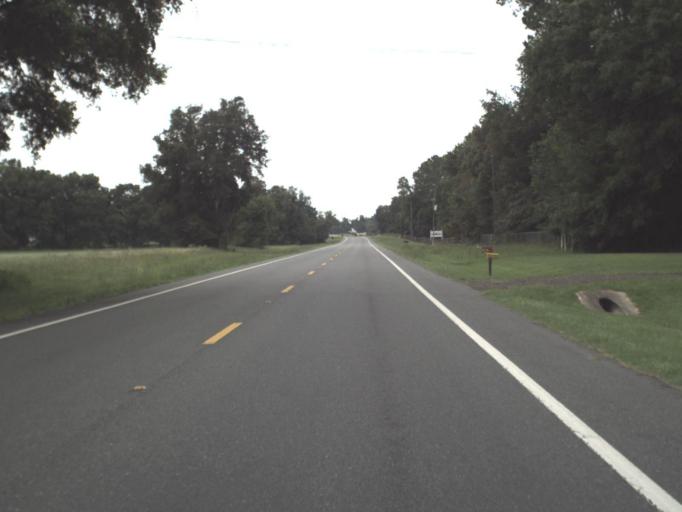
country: US
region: Florida
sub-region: Levy County
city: Williston
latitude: 29.3425
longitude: -82.4558
